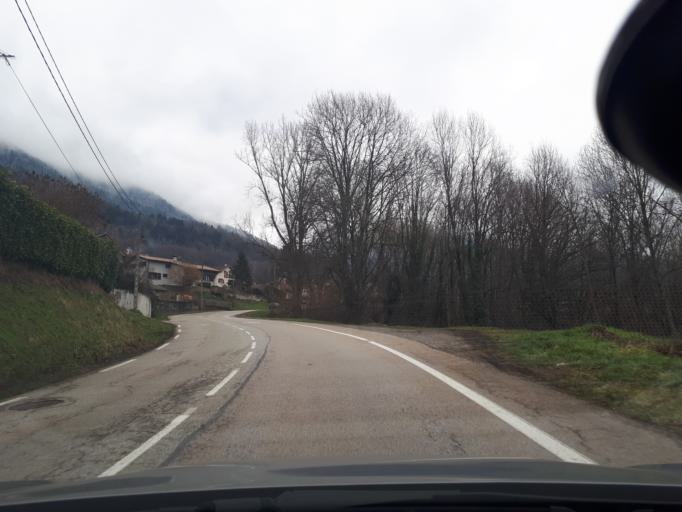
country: FR
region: Rhone-Alpes
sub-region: Departement de l'Isere
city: Vaulnaveys-le-Haut
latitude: 45.1231
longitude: 5.8280
